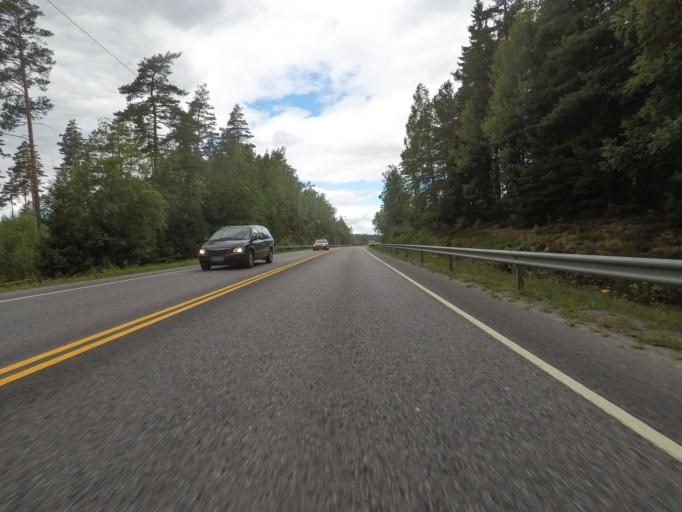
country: FI
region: Varsinais-Suomi
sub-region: Turku
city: Piikkioe
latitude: 60.4468
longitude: 22.4716
